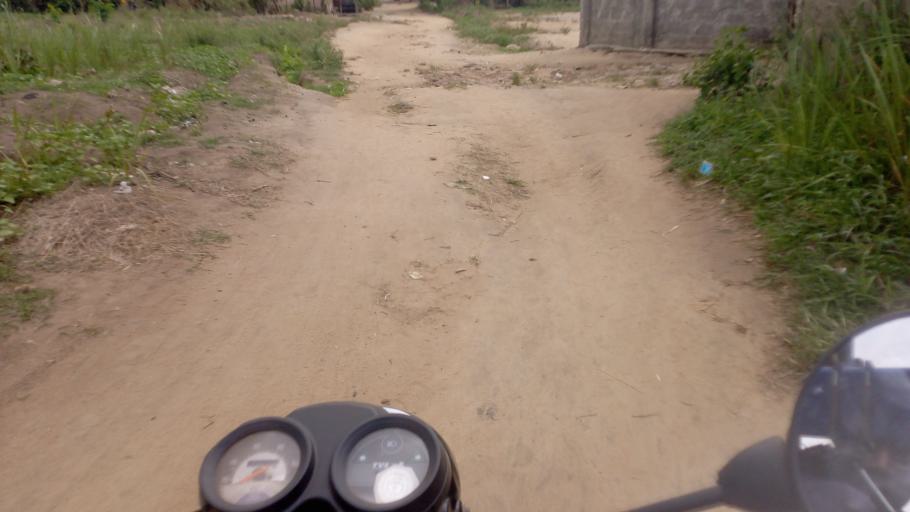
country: SL
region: Western Area
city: Waterloo
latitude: 8.3119
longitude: -13.0630
